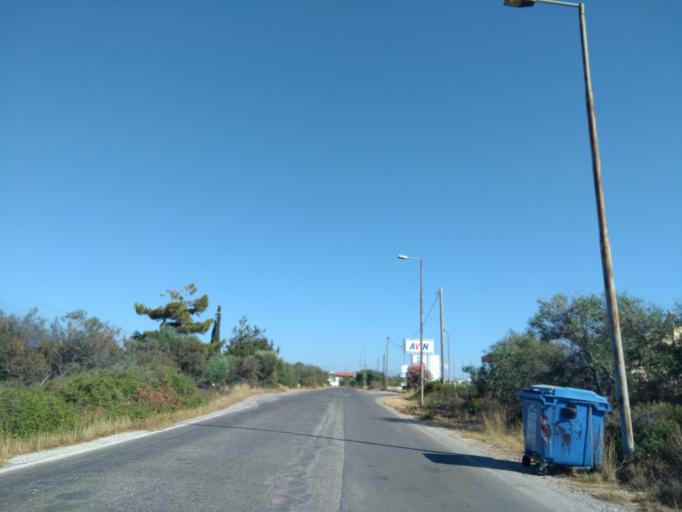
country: GR
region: Crete
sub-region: Nomos Chanias
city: Pithari
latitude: 35.5814
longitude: 24.0926
